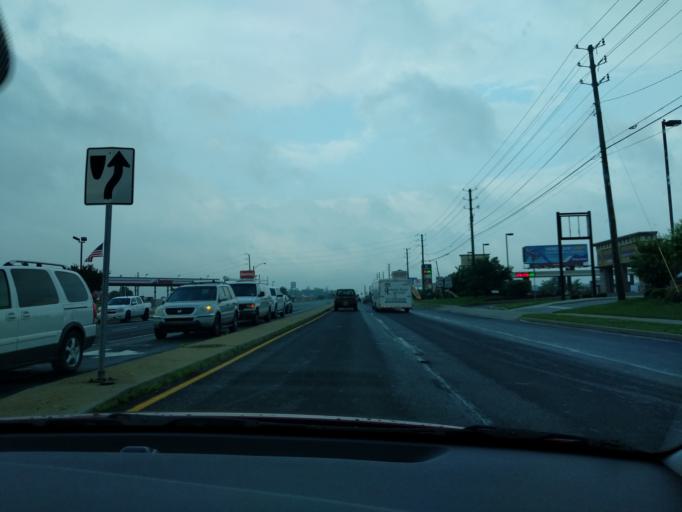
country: US
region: Indiana
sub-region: Marion County
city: Lawrence
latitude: 39.8625
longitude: -85.9729
